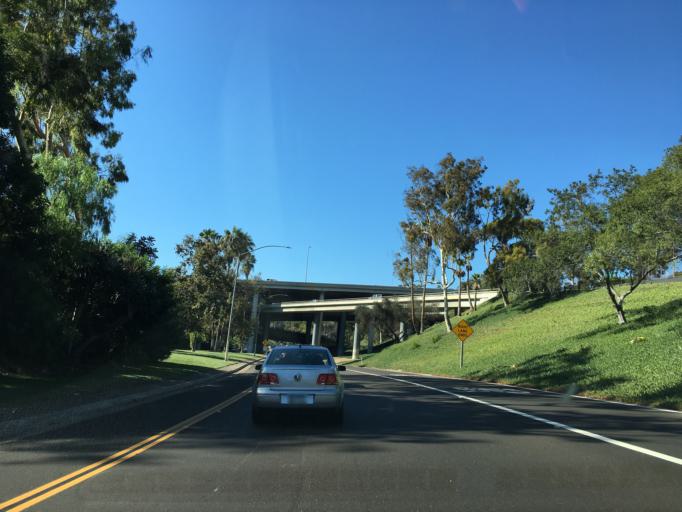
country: US
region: California
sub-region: San Diego County
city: San Diego
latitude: 32.7223
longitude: -117.1548
